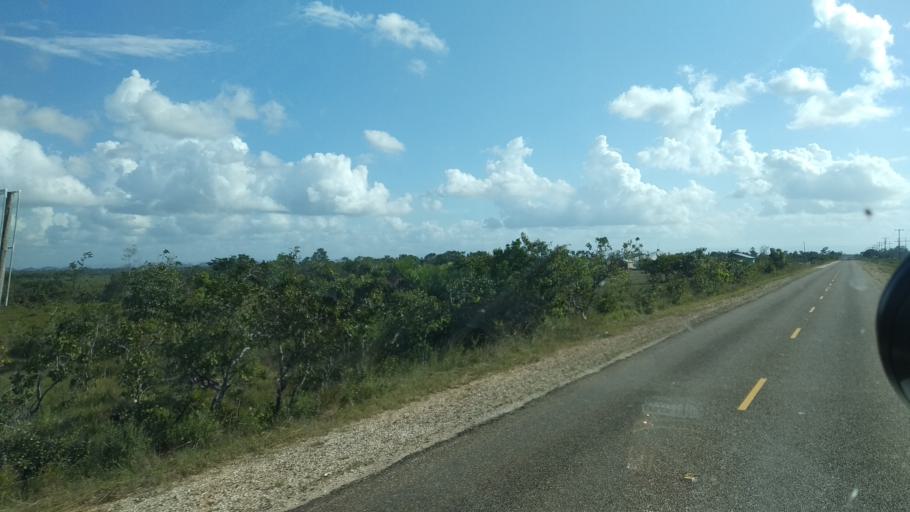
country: BZ
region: Cayo
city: Belmopan
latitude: 17.3969
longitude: -88.5086
